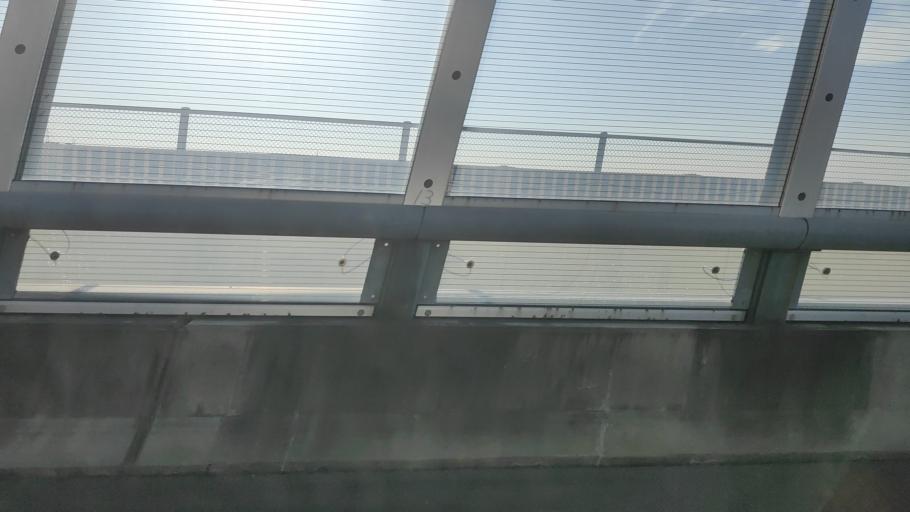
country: JP
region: Saitama
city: Yashio-shi
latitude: 35.8208
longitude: 139.8711
